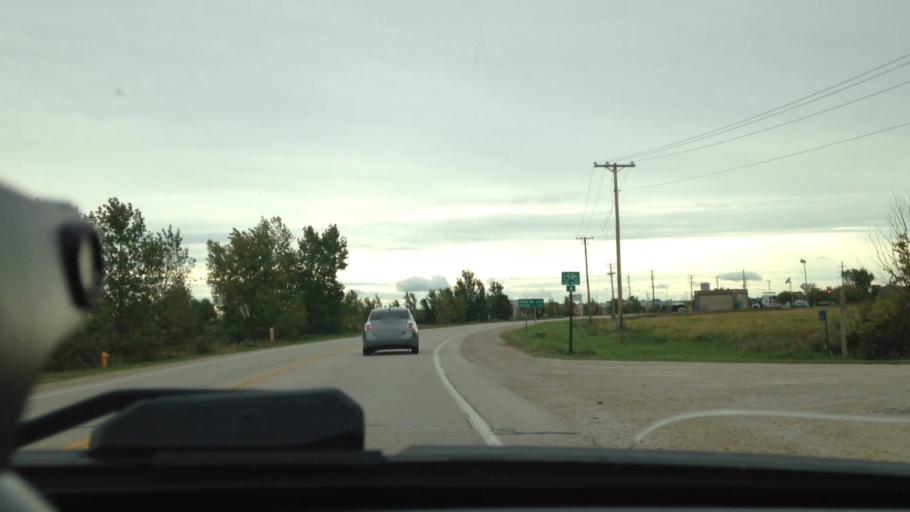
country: US
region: Wisconsin
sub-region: Fond du Lac County
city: North Fond du Lac
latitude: 43.7958
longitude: -88.4877
